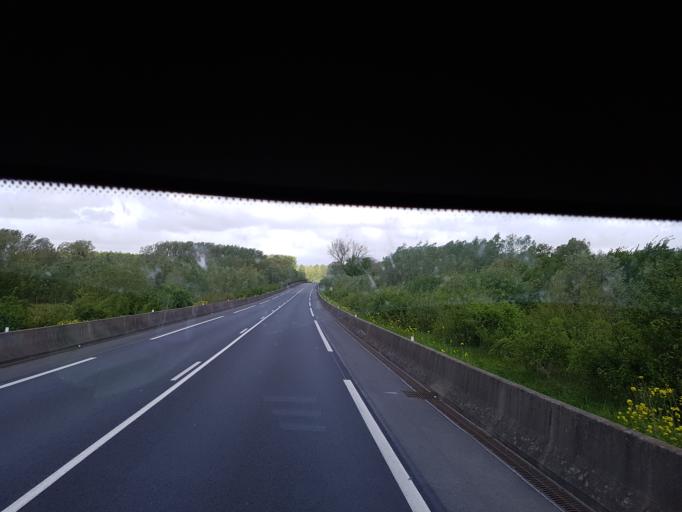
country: FR
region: Nord-Pas-de-Calais
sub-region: Departement du Nord
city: Proville
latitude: 50.1560
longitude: 3.1903
